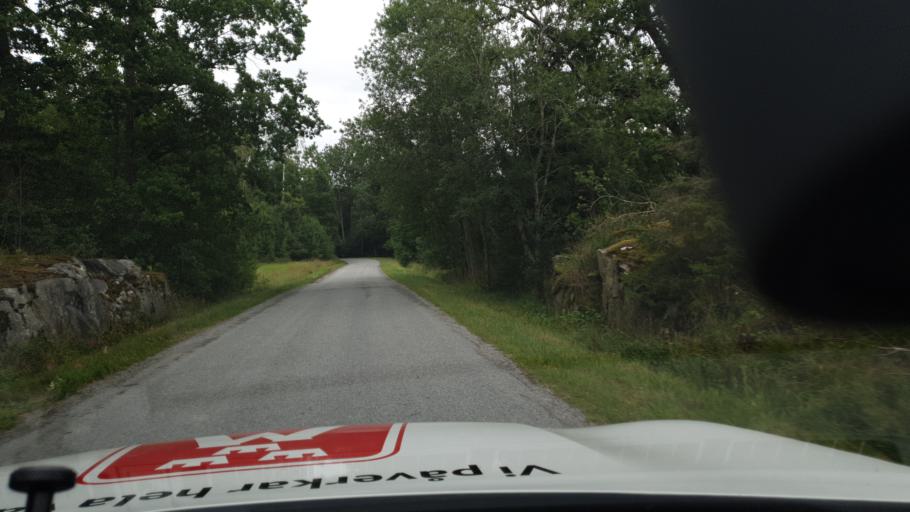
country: SE
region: Soedermanland
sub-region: Strangnas Kommun
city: Akers Styckebruk
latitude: 59.1825
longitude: 17.1452
